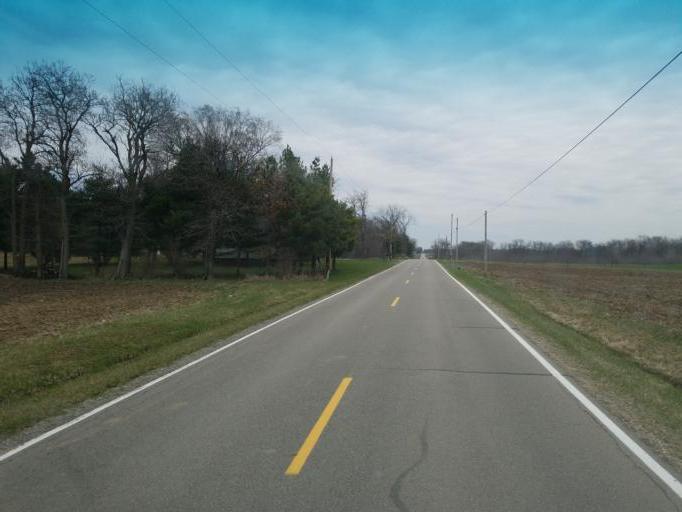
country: US
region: Ohio
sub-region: Crawford County
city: Bucyrus
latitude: 40.8920
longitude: -83.0285
